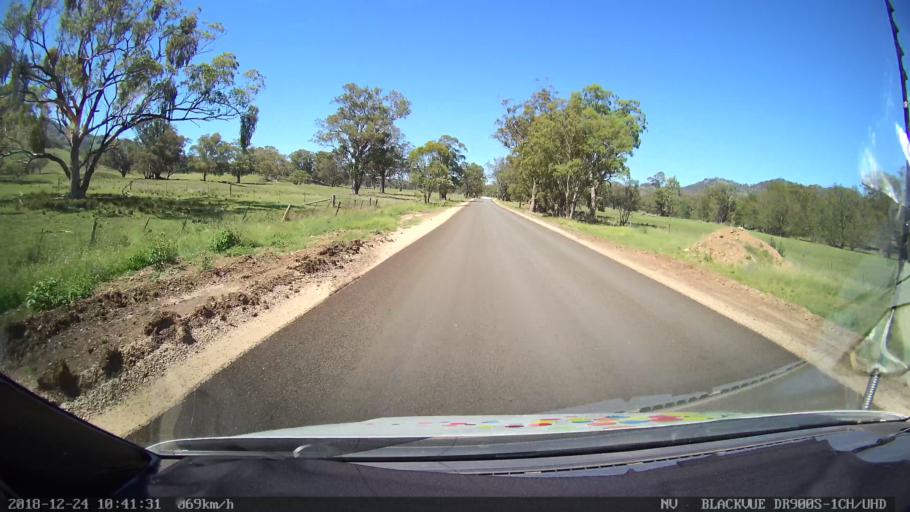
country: AU
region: New South Wales
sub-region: Upper Hunter Shire
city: Merriwa
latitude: -31.8695
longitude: 150.4586
